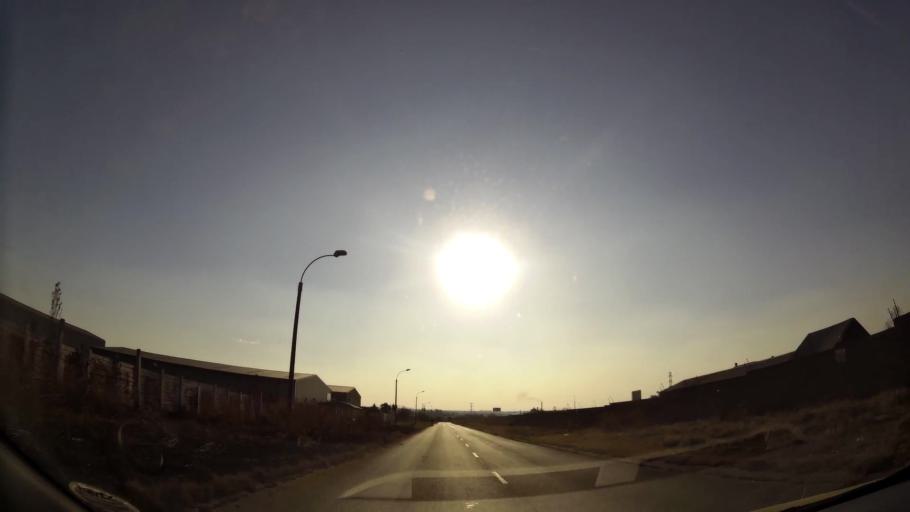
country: ZA
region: Gauteng
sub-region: West Rand District Municipality
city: Randfontein
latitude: -26.1952
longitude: 27.6932
